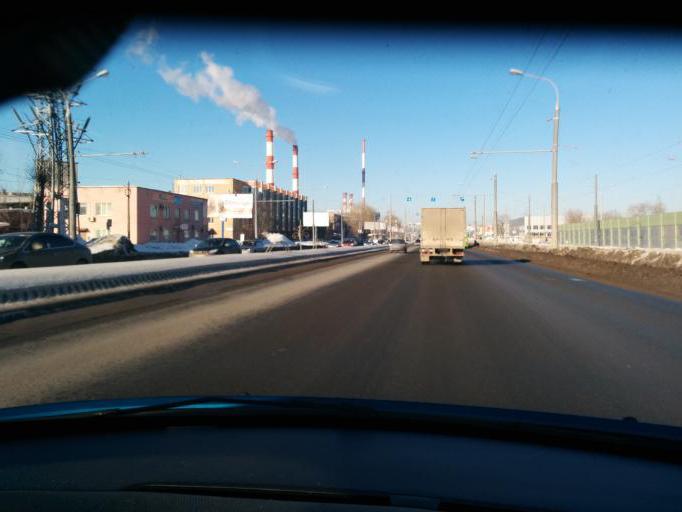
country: RU
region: Perm
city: Perm
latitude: 57.9716
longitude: 56.2609
